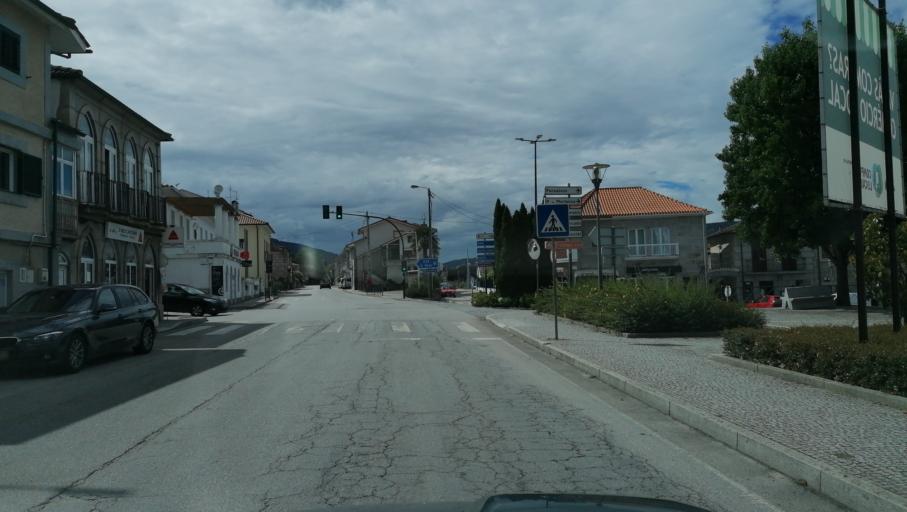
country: PT
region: Vila Real
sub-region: Vila Pouca de Aguiar
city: Vila Pouca de Aguiar
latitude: 41.5429
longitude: -7.6028
